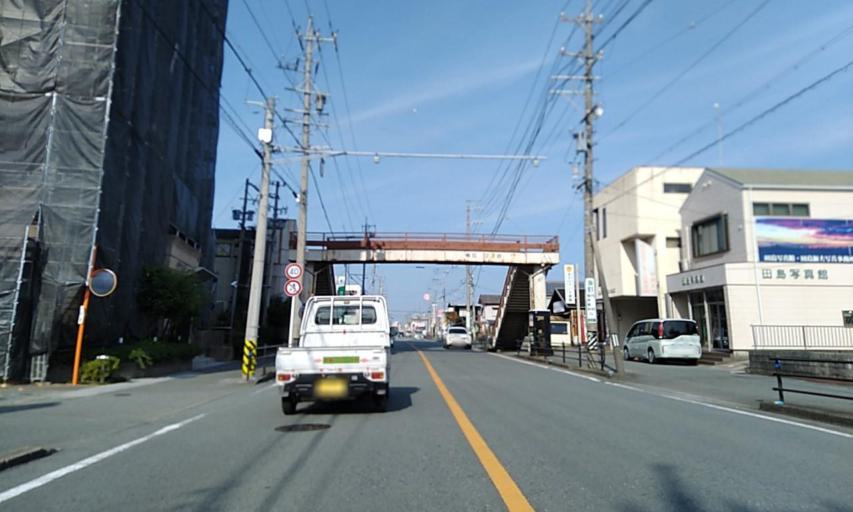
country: JP
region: Mie
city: Ise
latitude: 34.4966
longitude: 136.7146
